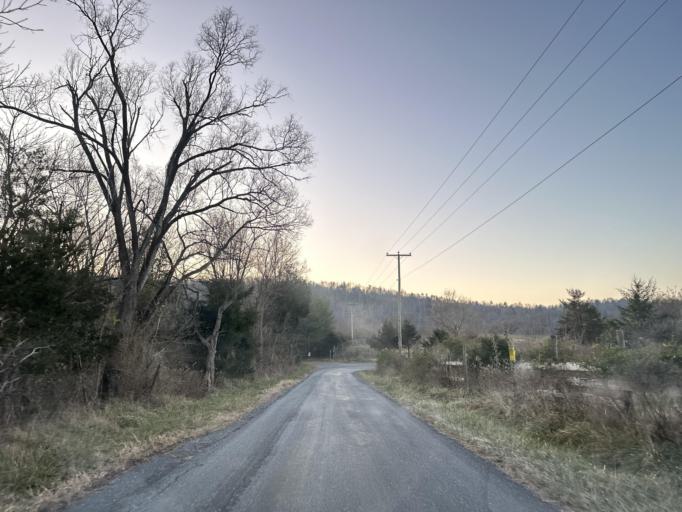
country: US
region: Virginia
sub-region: Augusta County
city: Jolivue
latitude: 38.0813
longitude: -79.3655
